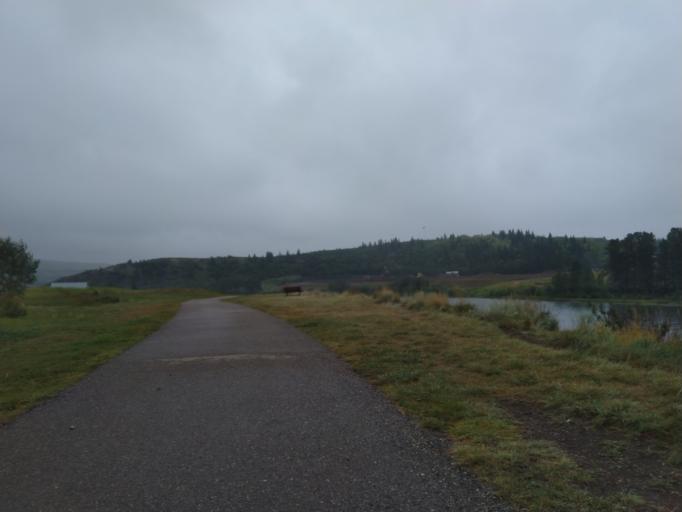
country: CA
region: Alberta
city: Cochrane
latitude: 51.1740
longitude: -114.4542
